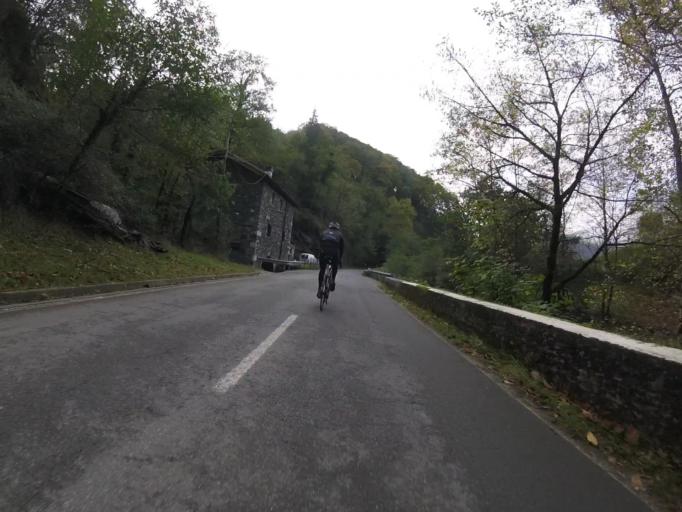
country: ES
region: Navarre
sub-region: Provincia de Navarra
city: Goizueta
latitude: 43.1775
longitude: -1.8616
